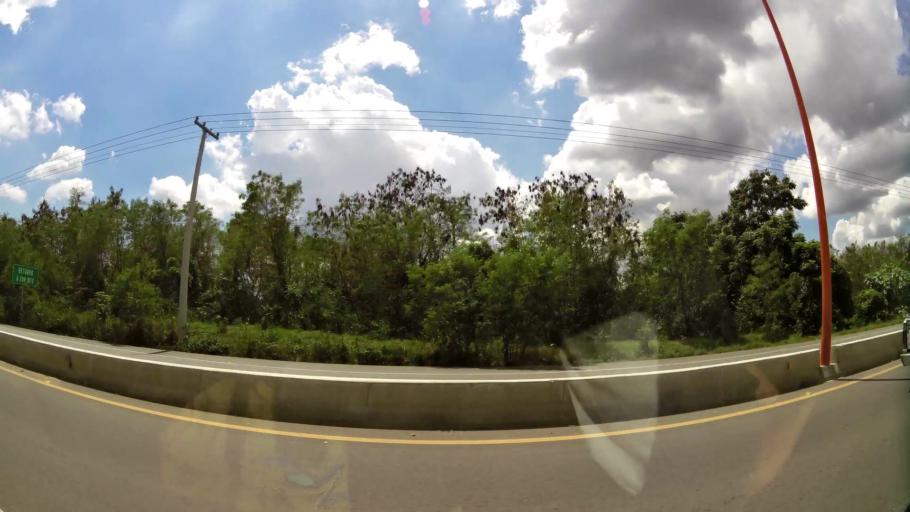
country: DO
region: Nacional
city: Santo Domingo
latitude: 18.5511
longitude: -69.9691
